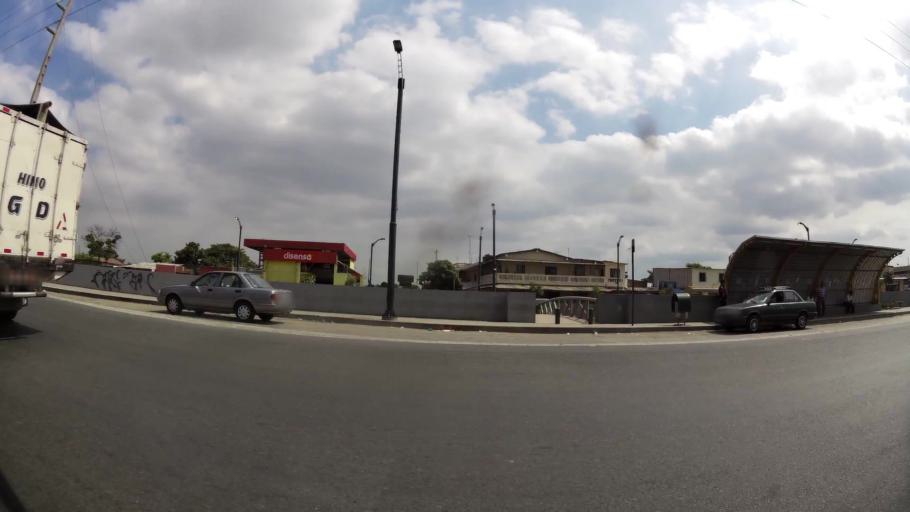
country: EC
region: Guayas
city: Eloy Alfaro
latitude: -2.0694
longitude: -79.9241
